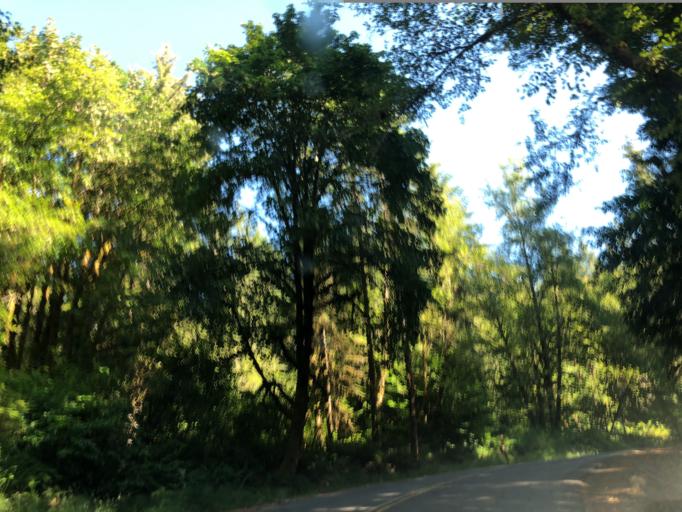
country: US
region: Oregon
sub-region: Linn County
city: Sweet Home
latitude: 44.4665
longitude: -122.6742
